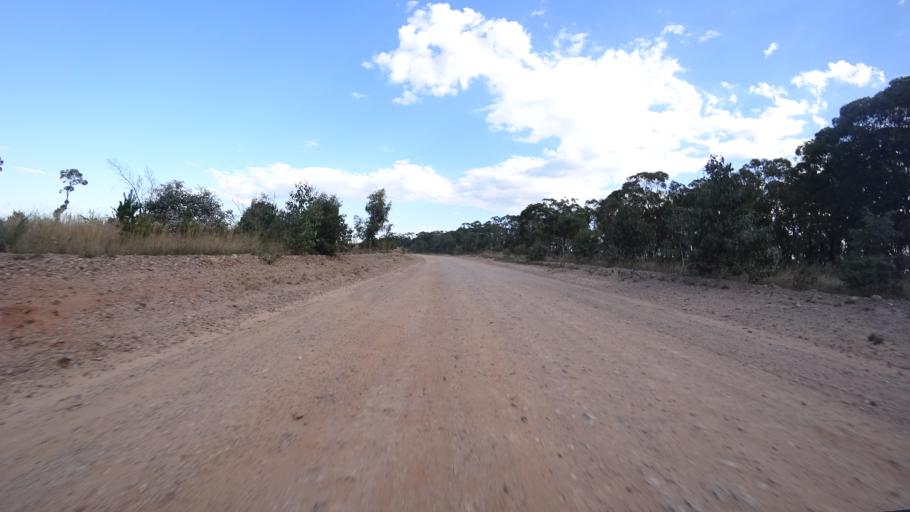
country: AU
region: New South Wales
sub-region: Lithgow
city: Lithgow
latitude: -33.4076
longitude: 150.1988
